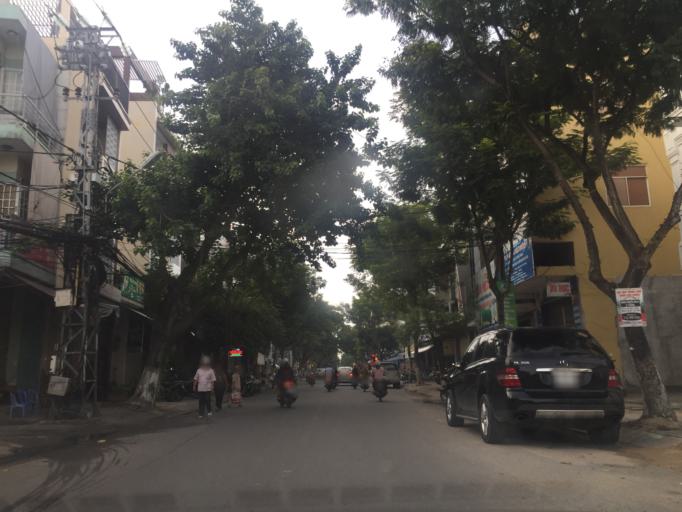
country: VN
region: Da Nang
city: Da Nang
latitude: 16.0743
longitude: 108.2126
